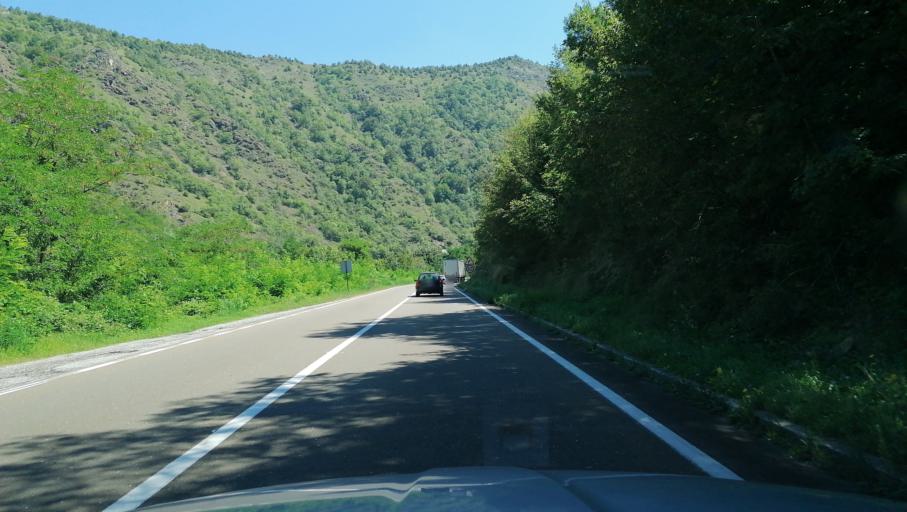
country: RS
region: Central Serbia
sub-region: Raski Okrug
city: Kraljevo
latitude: 43.5608
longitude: 20.6162
